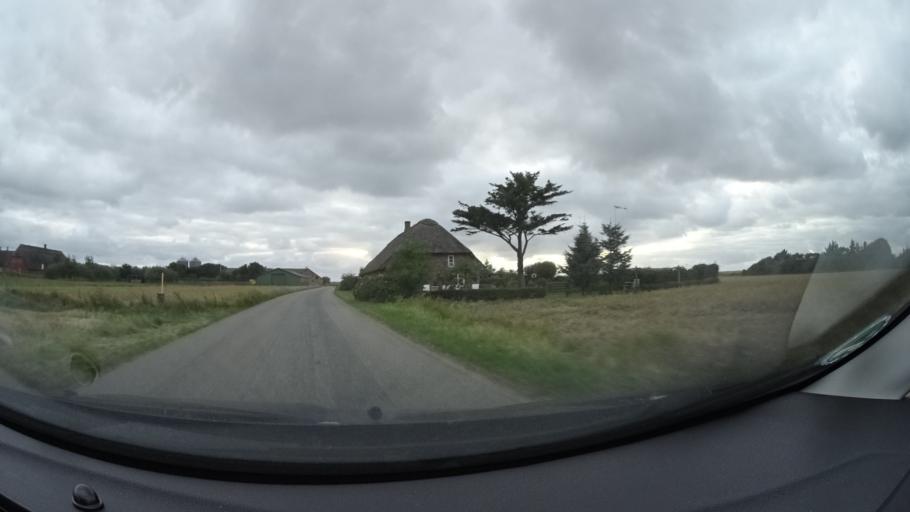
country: DK
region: Central Jutland
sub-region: Ringkobing-Skjern Kommune
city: Ringkobing
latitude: 56.1607
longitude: 8.1490
